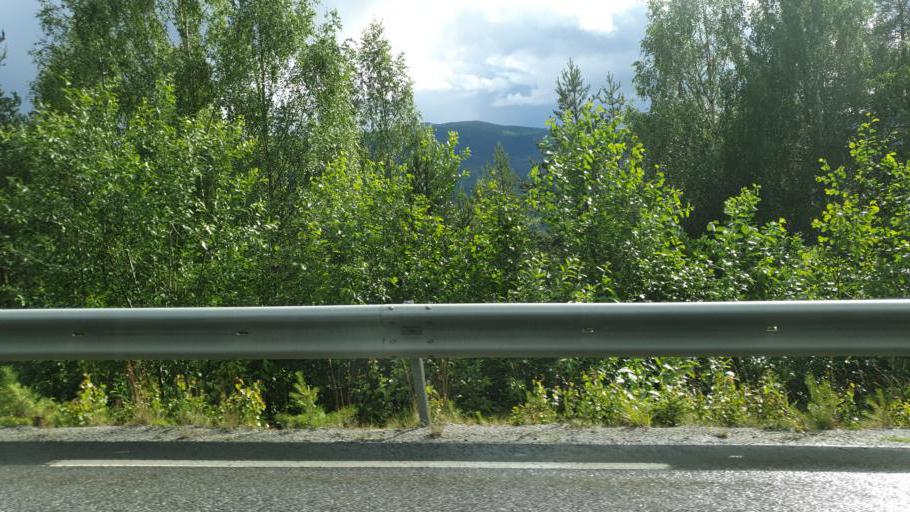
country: NO
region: Oppland
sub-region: Dovre
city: Dovre
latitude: 61.8682
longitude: 9.2237
